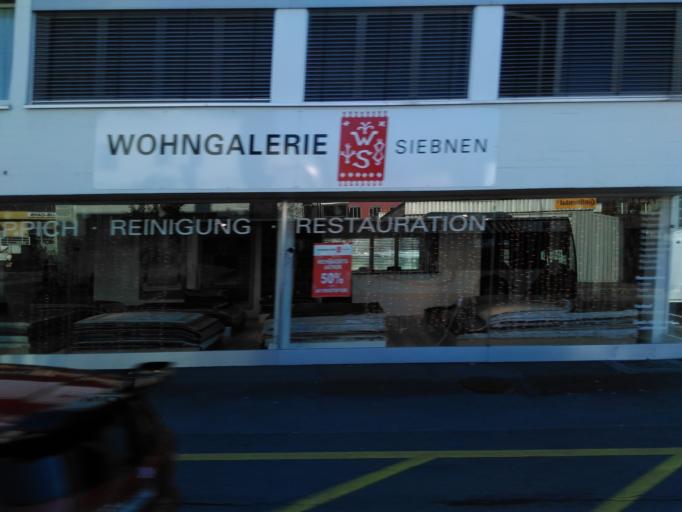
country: CH
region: Schwyz
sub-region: Bezirk March
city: Schubelbach
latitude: 47.1762
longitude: 8.8930
